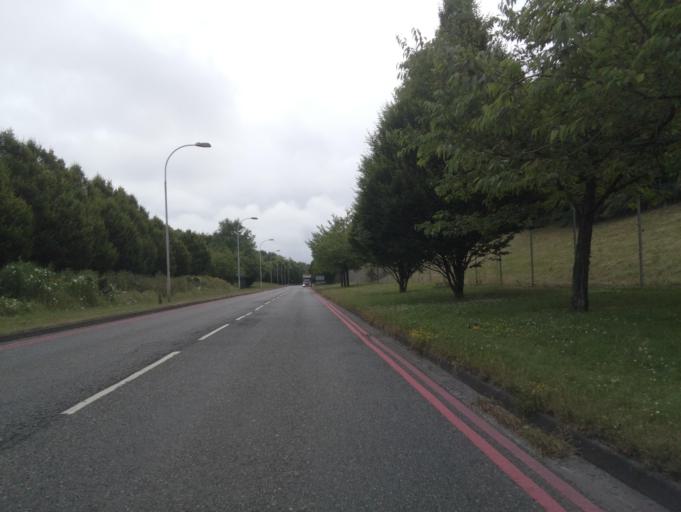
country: GB
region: England
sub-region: Surrey
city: Horley
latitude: 51.1642
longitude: -0.1808
